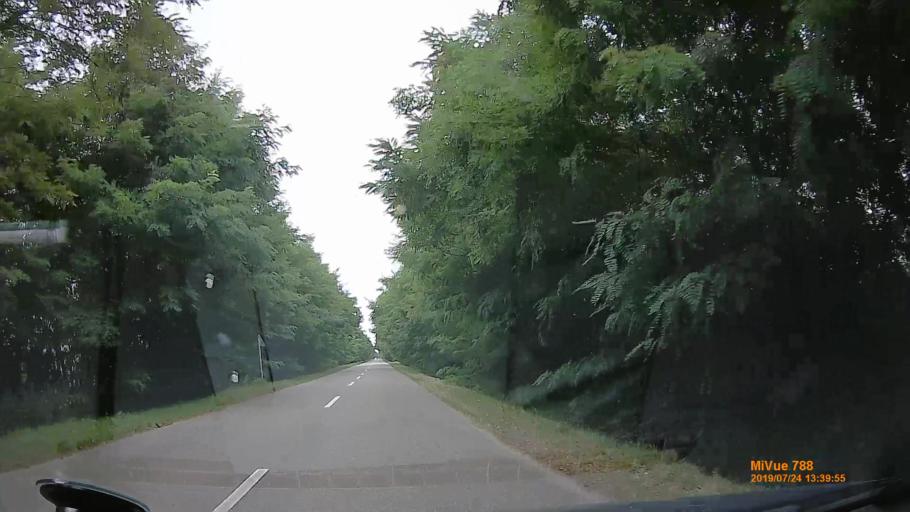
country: HU
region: Szabolcs-Szatmar-Bereg
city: Aranyosapati
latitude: 48.2451
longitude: 22.3159
